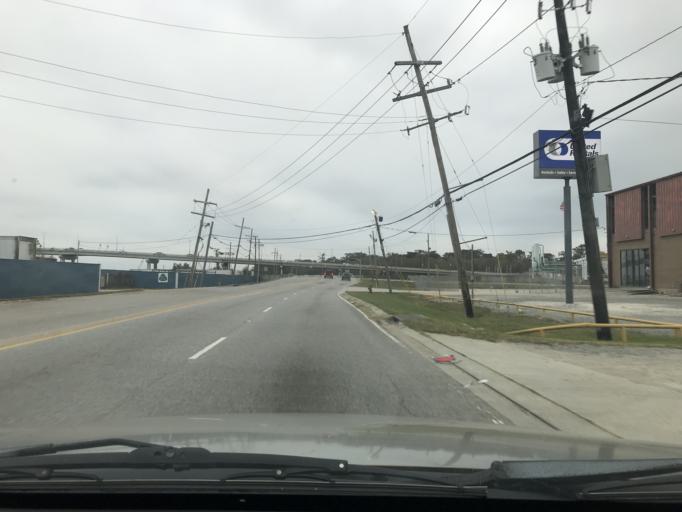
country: US
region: Louisiana
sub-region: Jefferson Parish
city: Woodmere
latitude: 29.8732
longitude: -90.0729
